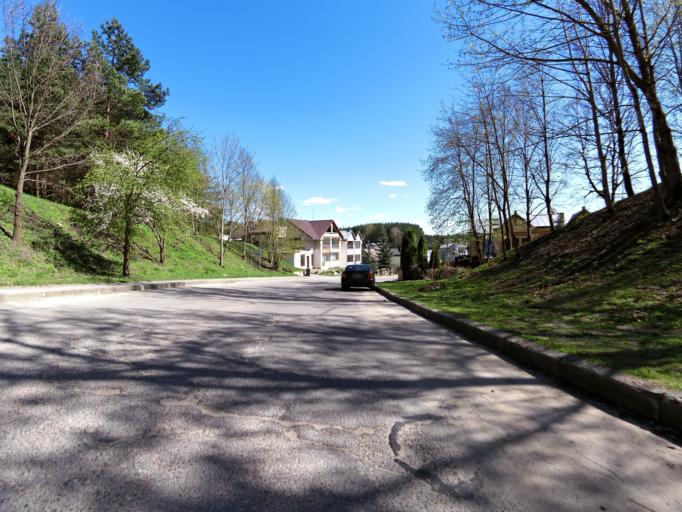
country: LT
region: Vilnius County
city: Rasos
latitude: 54.6885
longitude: 25.3149
